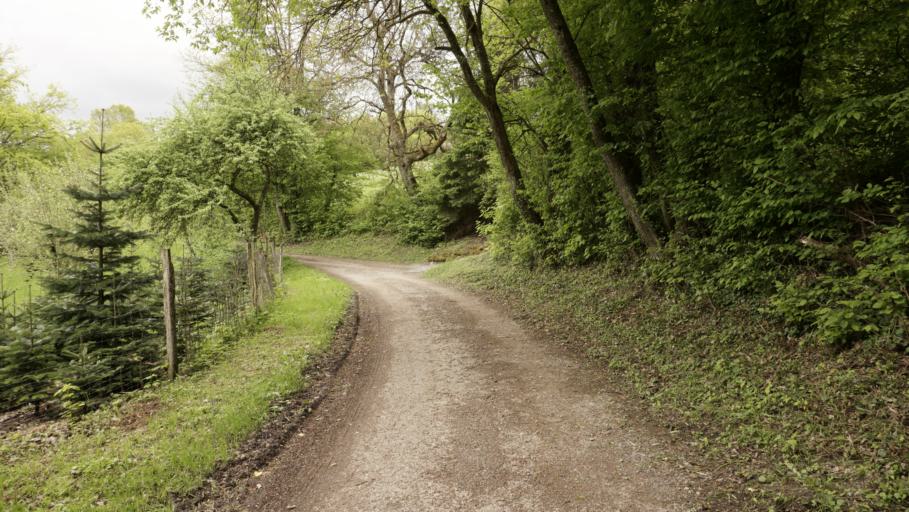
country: DE
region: Baden-Wuerttemberg
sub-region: Karlsruhe Region
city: Mosbach
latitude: 49.3700
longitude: 9.1734
